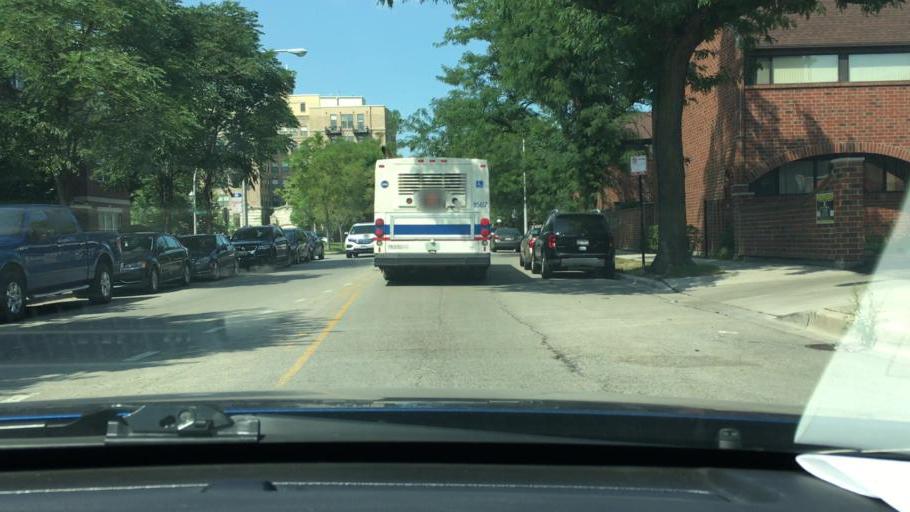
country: US
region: Illinois
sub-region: Cook County
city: Chicago
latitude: 41.8699
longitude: -87.6568
